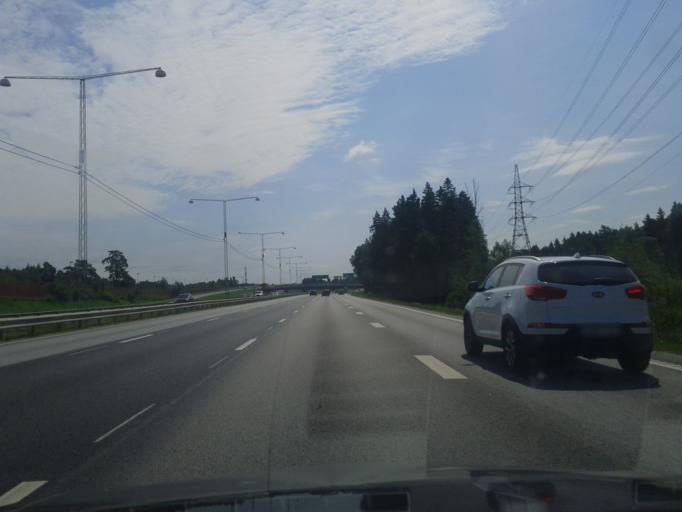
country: SE
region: Stockholm
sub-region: Stockholms Kommun
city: Kista
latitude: 59.4069
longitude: 17.9617
